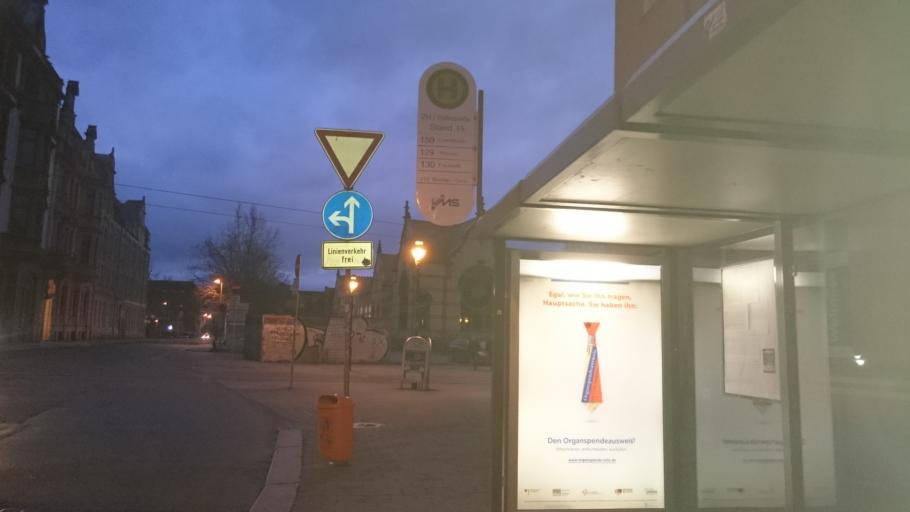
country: DE
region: Saxony
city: Zwickau
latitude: 50.7183
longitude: 12.4869
